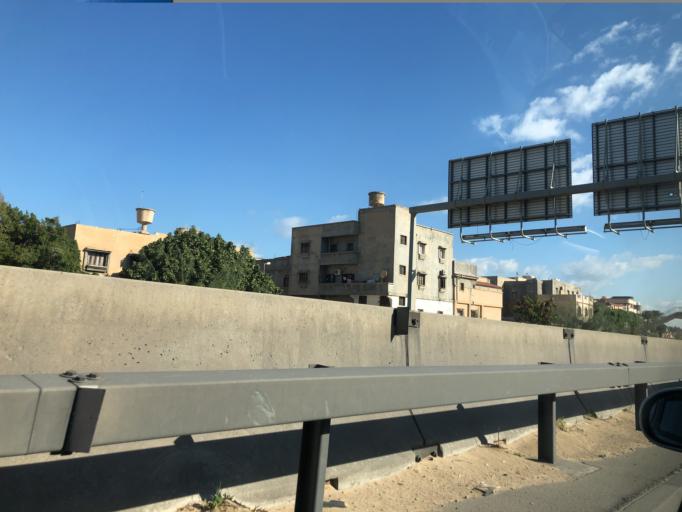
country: LY
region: Tripoli
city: Tripoli
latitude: 32.8564
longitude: 13.2050
